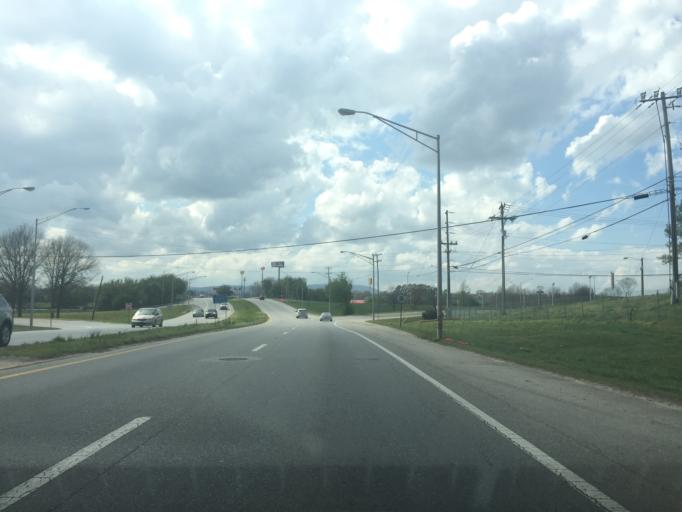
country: US
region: Georgia
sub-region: Catoosa County
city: Indian Springs
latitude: 34.9901
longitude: -85.2000
